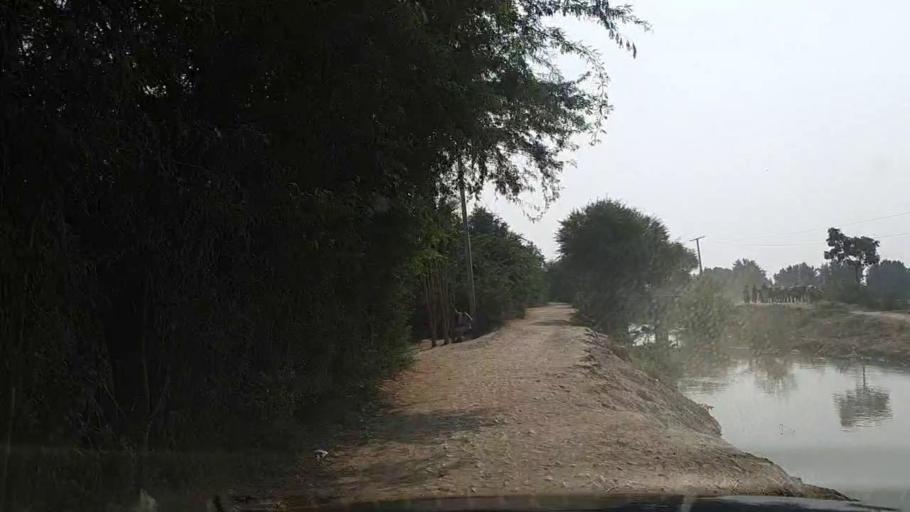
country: PK
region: Sindh
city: Mirpur Batoro
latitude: 24.6966
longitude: 68.2192
